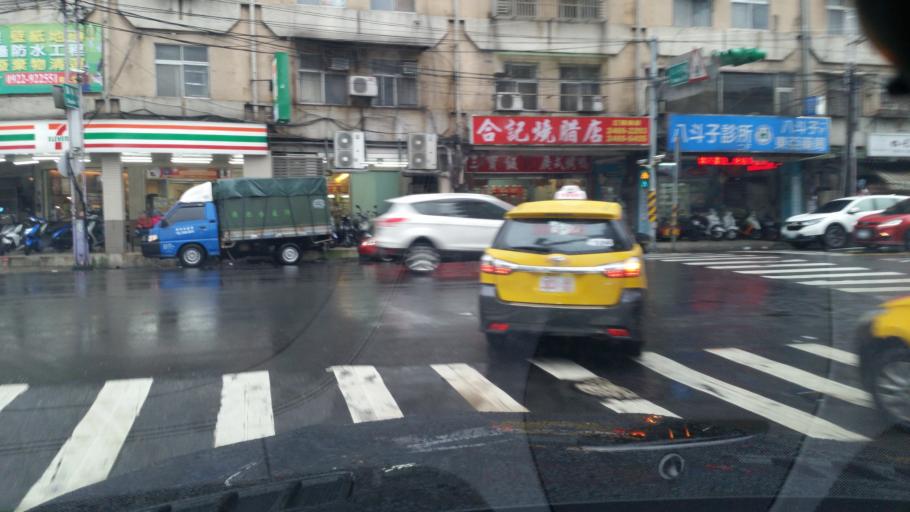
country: TW
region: Taiwan
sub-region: Keelung
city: Keelung
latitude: 25.1397
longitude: 121.7961
